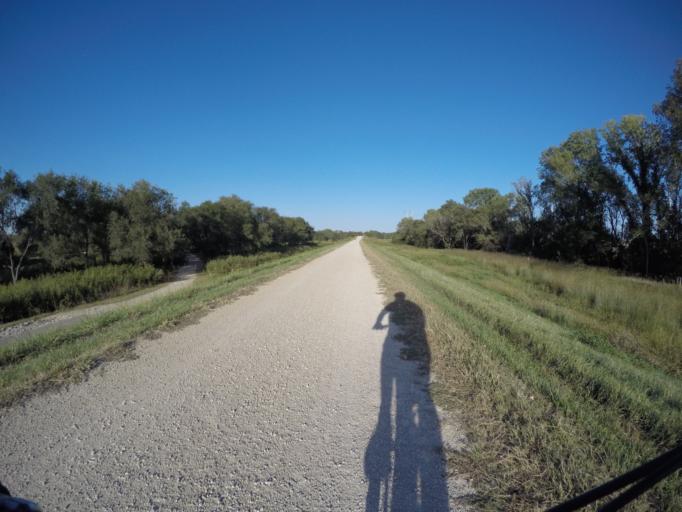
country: US
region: Kansas
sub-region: Riley County
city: Manhattan
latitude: 39.1962
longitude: -96.5496
